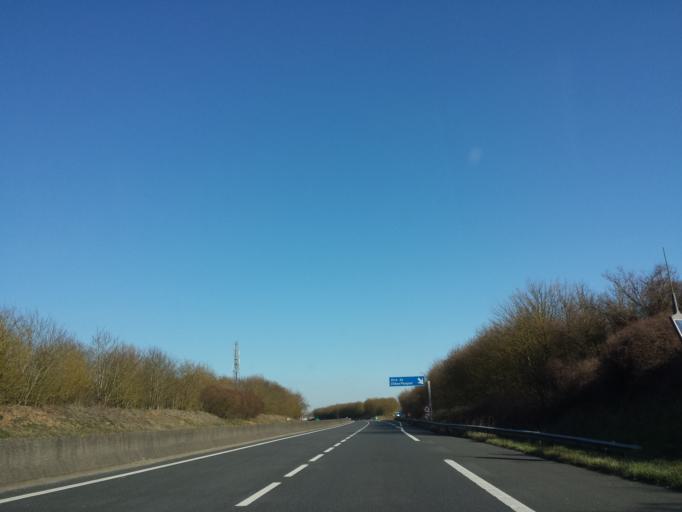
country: FR
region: Picardie
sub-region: Departement de l'Oise
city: Tille
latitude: 49.4628
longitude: 2.1588
